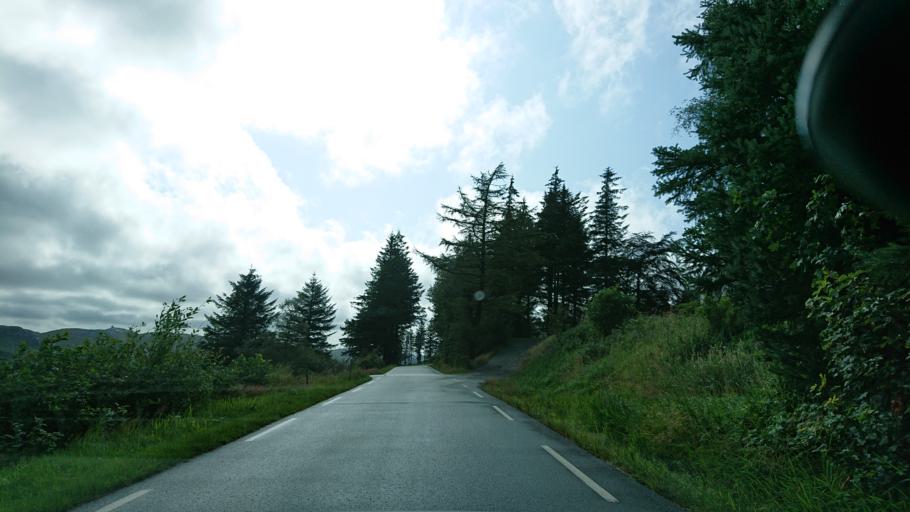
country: NO
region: Rogaland
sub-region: Gjesdal
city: Algard
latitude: 58.6834
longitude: 5.8631
